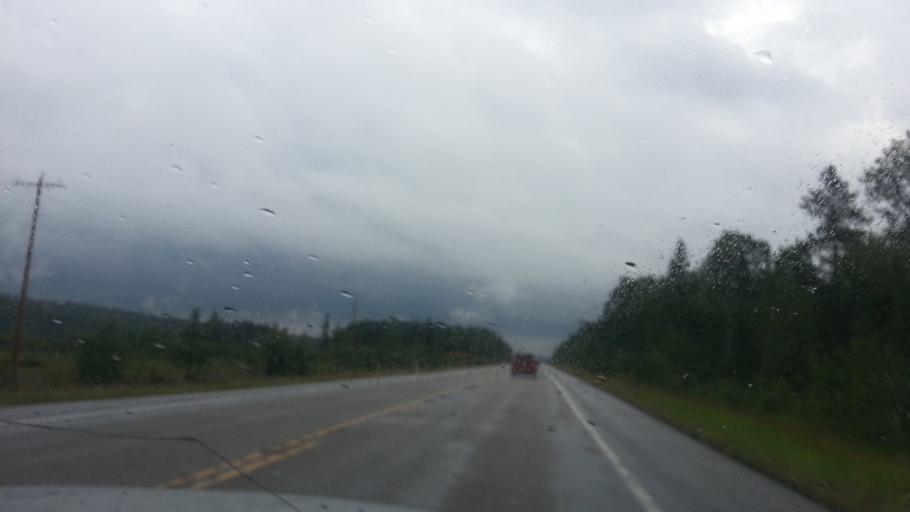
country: CA
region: Alberta
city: Cochrane
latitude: 50.9214
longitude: -114.5997
